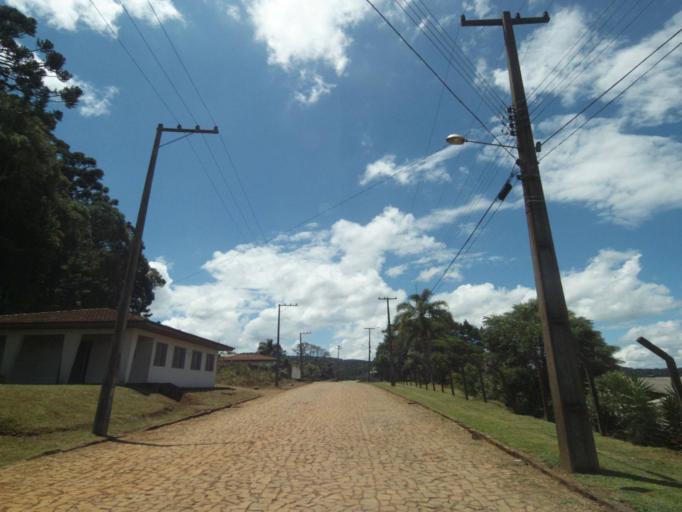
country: BR
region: Parana
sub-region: Uniao Da Vitoria
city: Uniao da Vitoria
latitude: -26.1616
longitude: -51.5564
